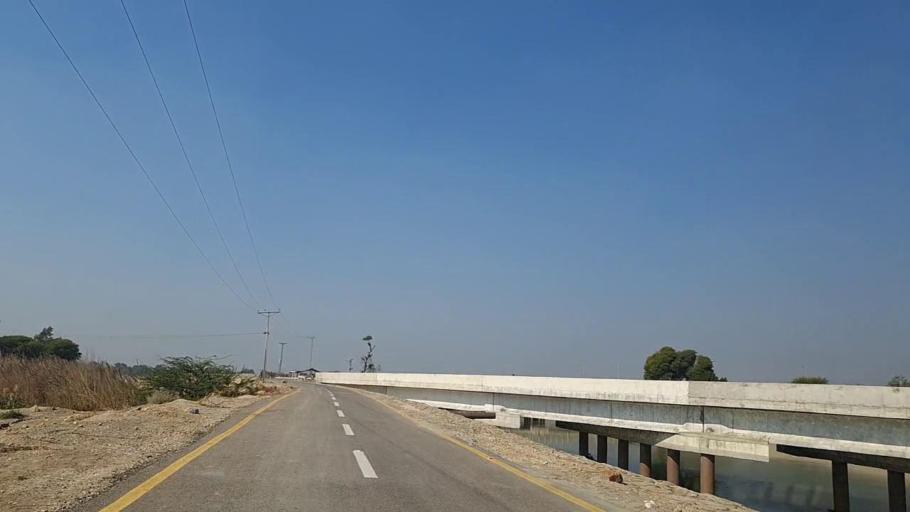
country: PK
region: Sindh
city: Sakrand
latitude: 26.2443
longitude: 68.2633
